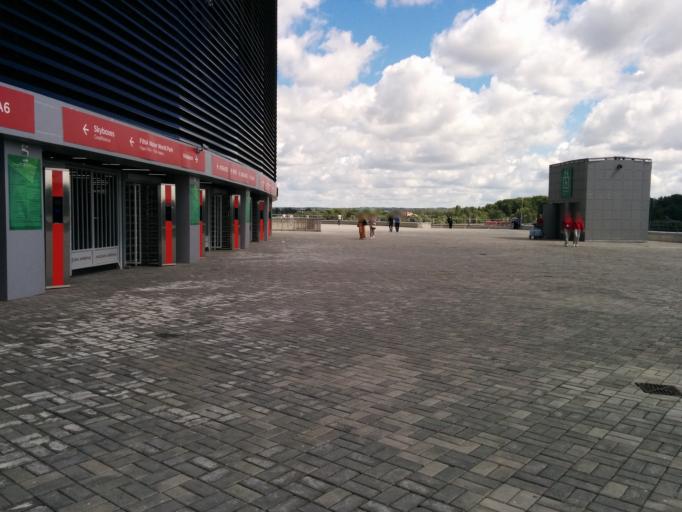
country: RU
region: Tatarstan
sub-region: Gorod Kazan'
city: Kazan
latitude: 55.8200
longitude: 49.1618
